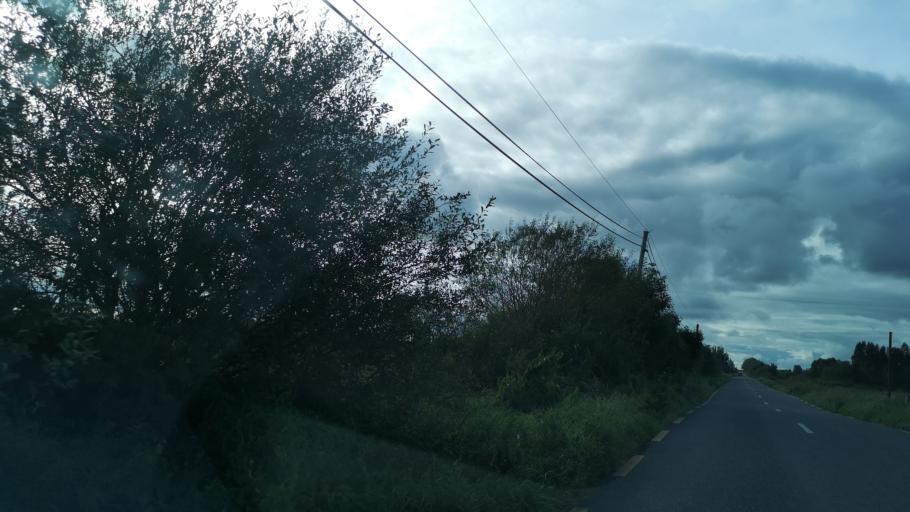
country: IE
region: Leinster
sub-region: Uibh Fhaili
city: Banagher
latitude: 53.2842
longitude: -8.0746
